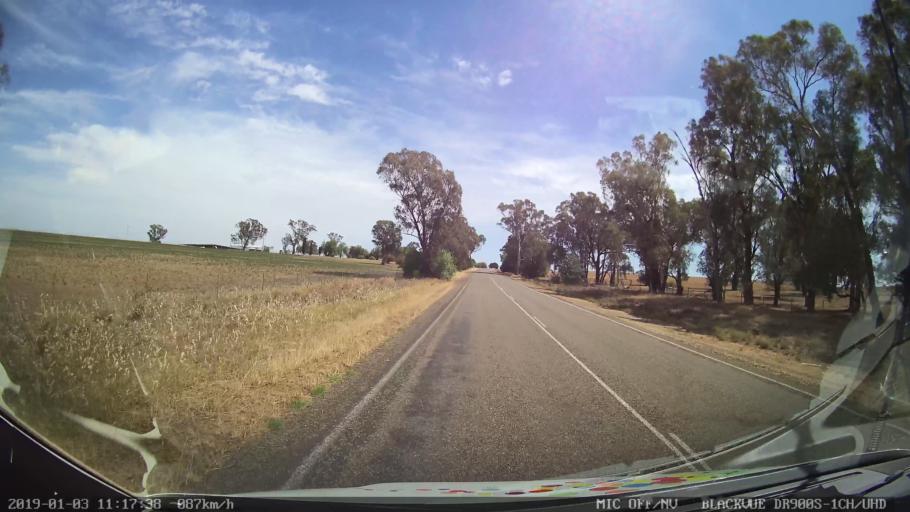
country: AU
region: New South Wales
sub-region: Young
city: Young
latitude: -34.1362
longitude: 148.2651
